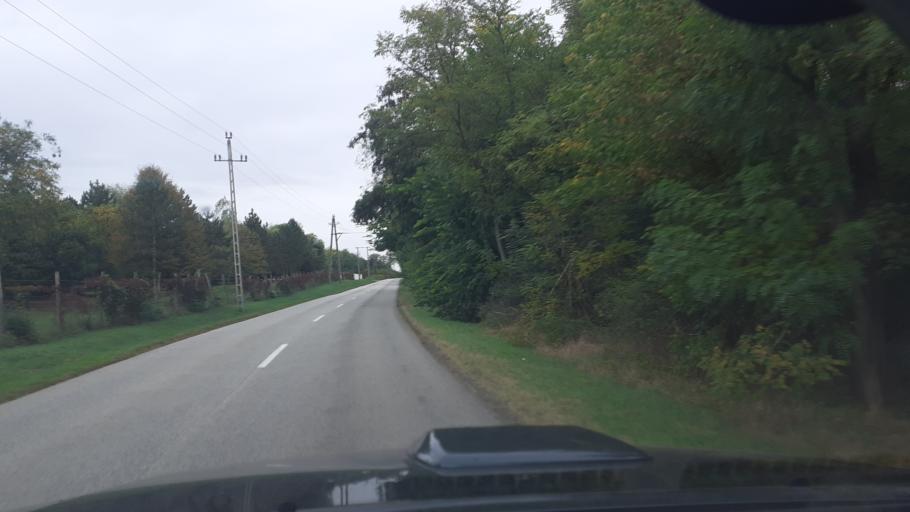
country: HU
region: Tolna
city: Dunafoldvar
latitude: 46.8328
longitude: 18.9025
